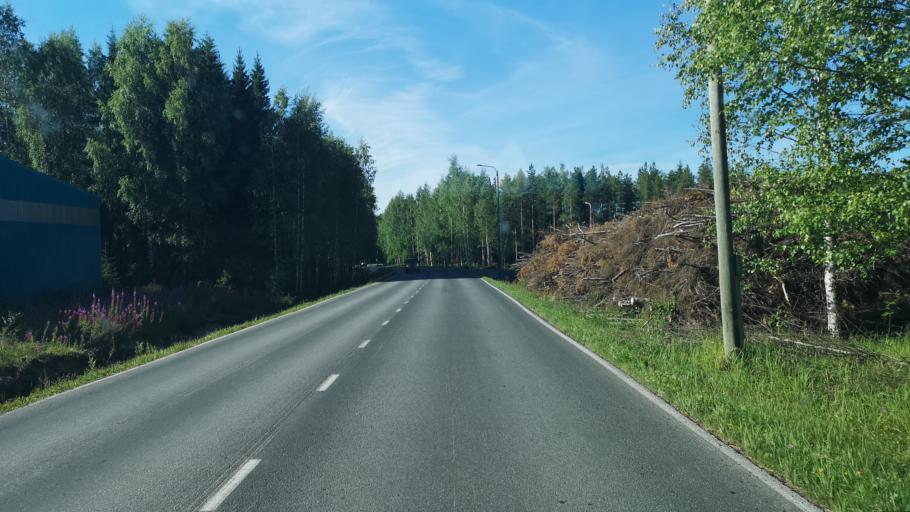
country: FI
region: Southern Ostrobothnia
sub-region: Seinaejoki
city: Lapua
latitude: 62.9720
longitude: 23.0544
